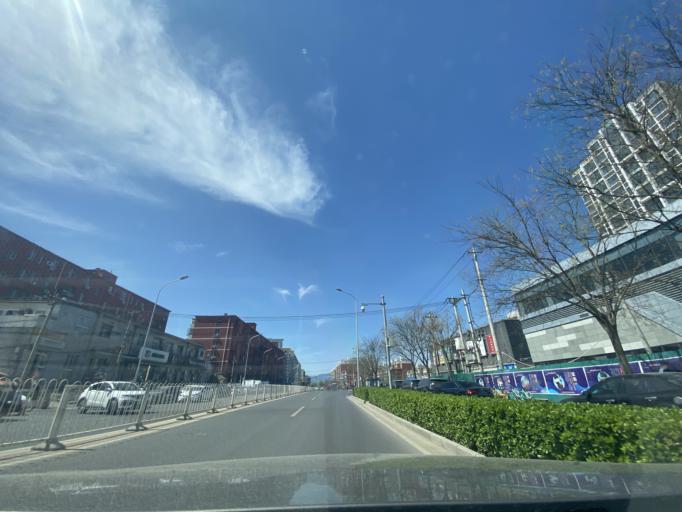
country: CN
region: Beijing
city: Sijiqing
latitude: 39.9283
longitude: 116.2493
